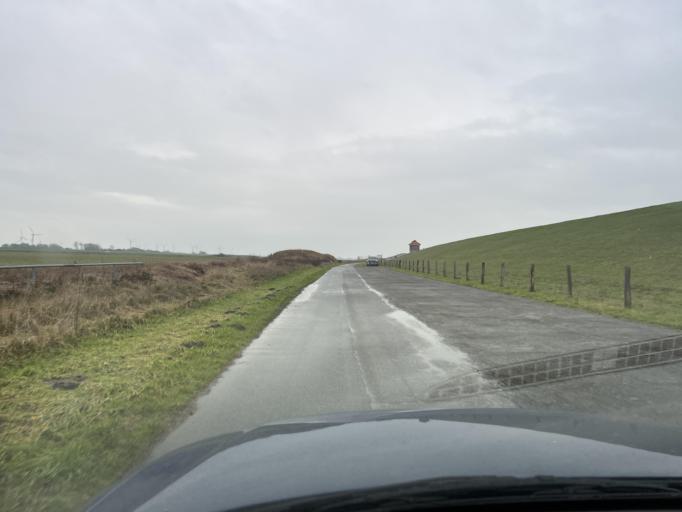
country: DE
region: Schleswig-Holstein
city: Hellschen-Heringsand-Unterschaar
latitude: 54.2227
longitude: 8.8418
